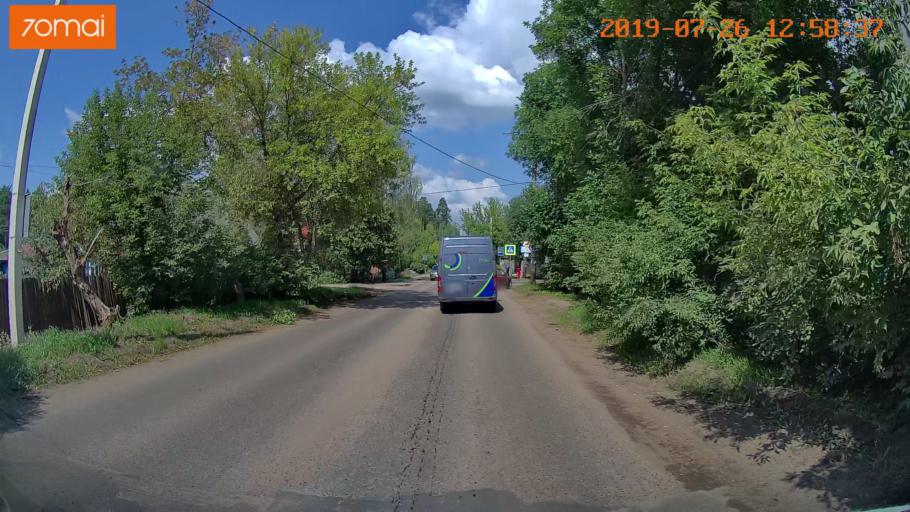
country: RU
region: Ivanovo
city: Bogorodskoye
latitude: 57.0252
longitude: 41.0208
